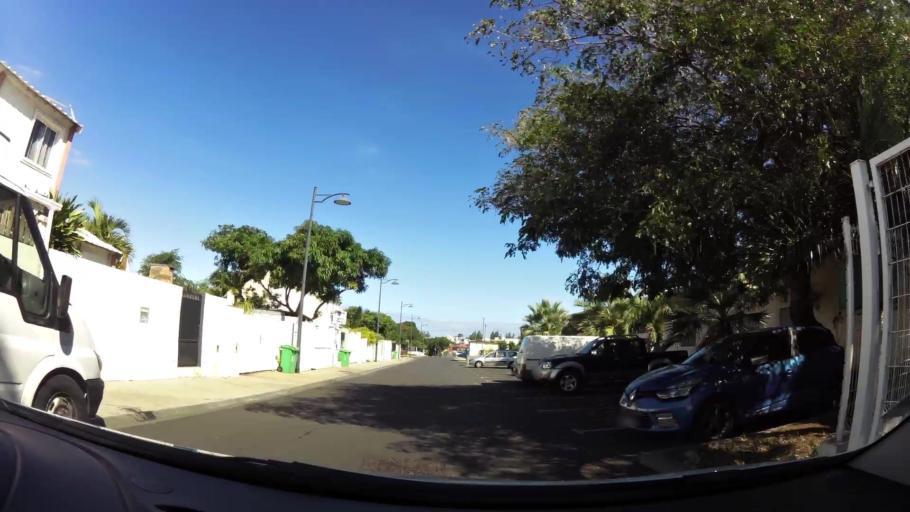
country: RE
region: Reunion
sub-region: Reunion
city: Saint-Pierre
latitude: -21.3373
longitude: 55.4622
